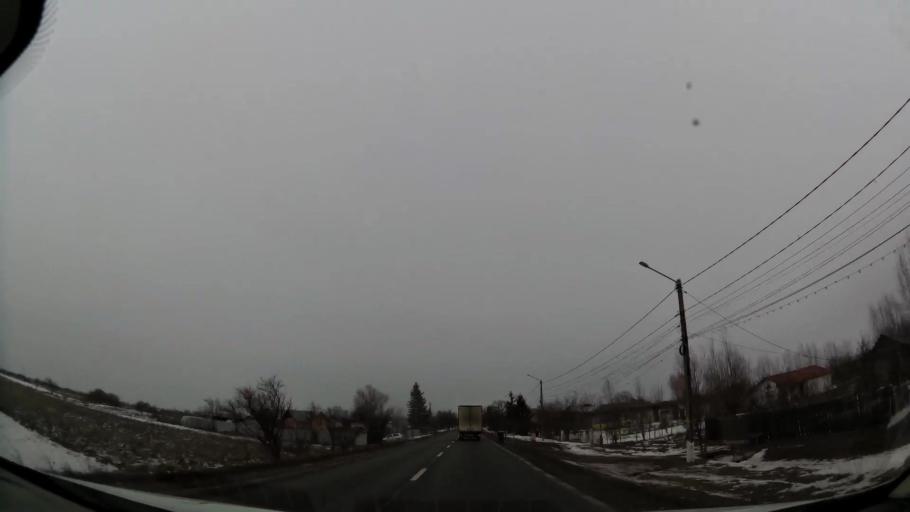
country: RO
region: Dambovita
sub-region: Comuna Tartasesti
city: Baldana
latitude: 44.5959
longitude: 25.7859
